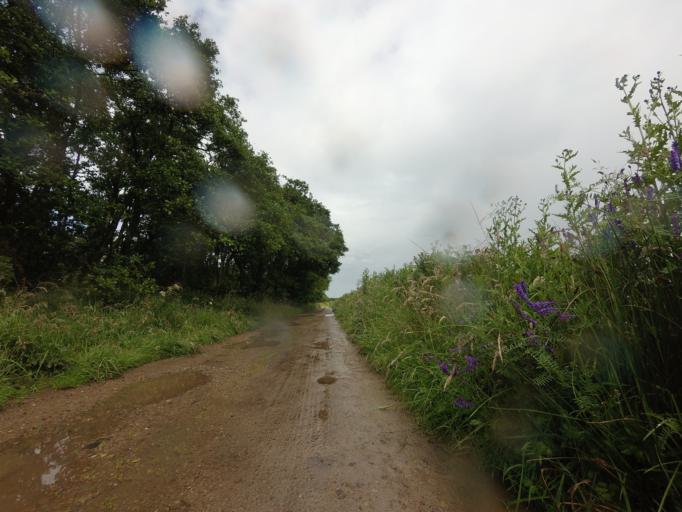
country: GB
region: Scotland
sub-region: Moray
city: Fochabers
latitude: 57.6632
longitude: -3.0906
